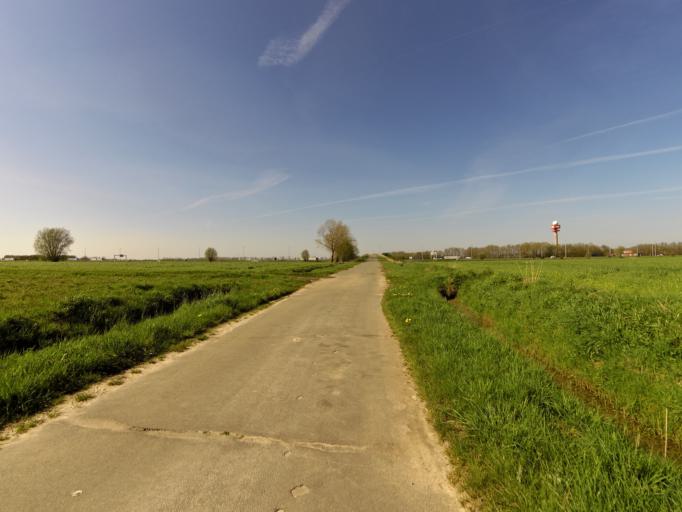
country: BE
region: Flanders
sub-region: Provincie West-Vlaanderen
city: Jabbeke
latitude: 51.1870
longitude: 3.0633
